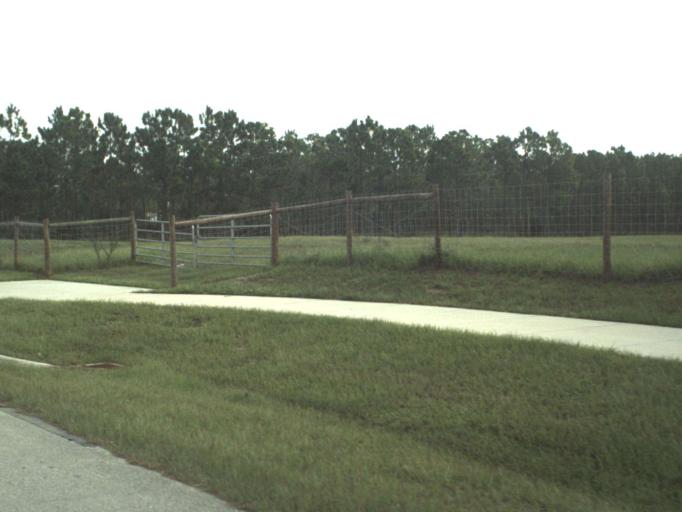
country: US
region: Florida
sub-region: Saint Lucie County
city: White City
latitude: 27.3520
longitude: -80.3558
